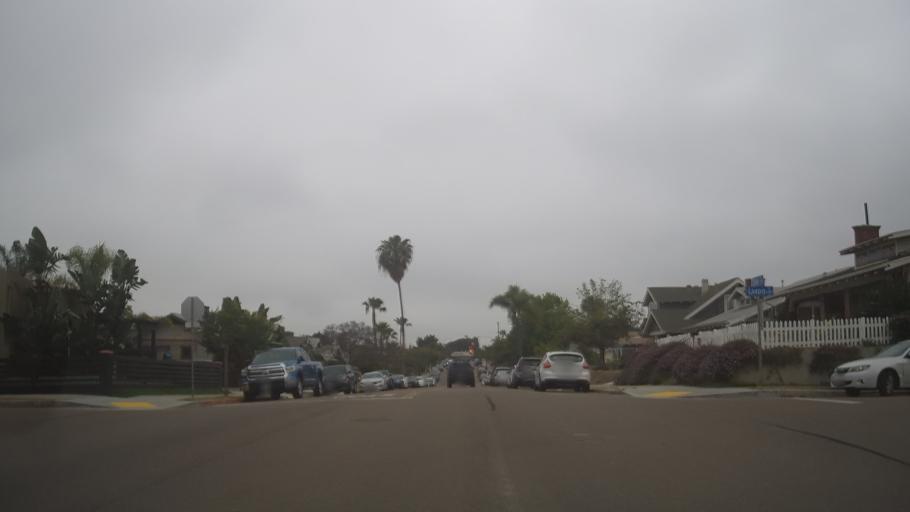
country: US
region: California
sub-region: San Diego County
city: San Diego
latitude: 32.7454
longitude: -117.1390
